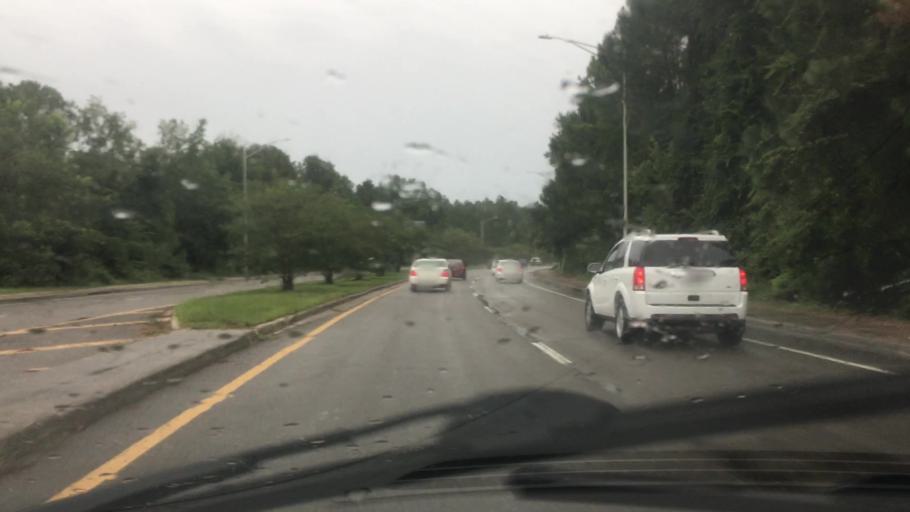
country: US
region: Florida
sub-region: Duval County
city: Jacksonville Beach
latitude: 30.2708
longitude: -81.5242
